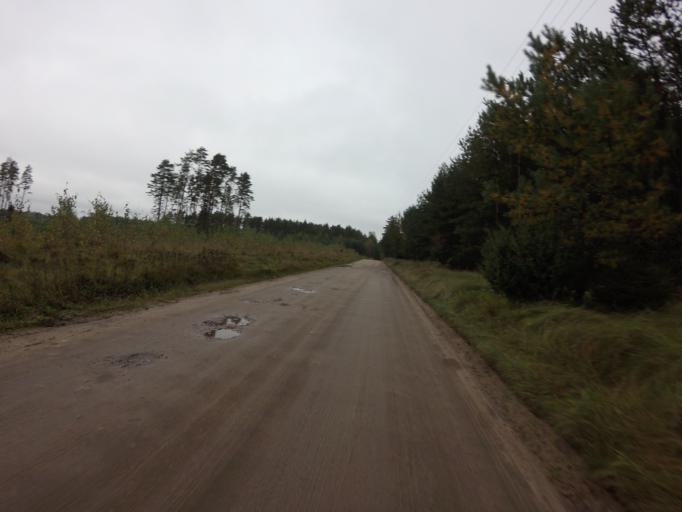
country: PL
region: Pomeranian Voivodeship
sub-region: Powiat kartuski
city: Stezyca
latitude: 54.1553
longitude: 17.9163
